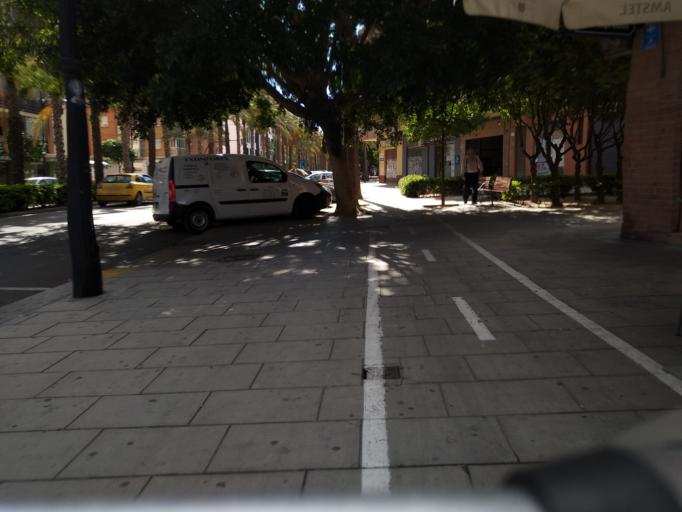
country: ES
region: Valencia
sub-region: Provincia de Valencia
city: Valencia
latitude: 39.4858
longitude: -0.3787
